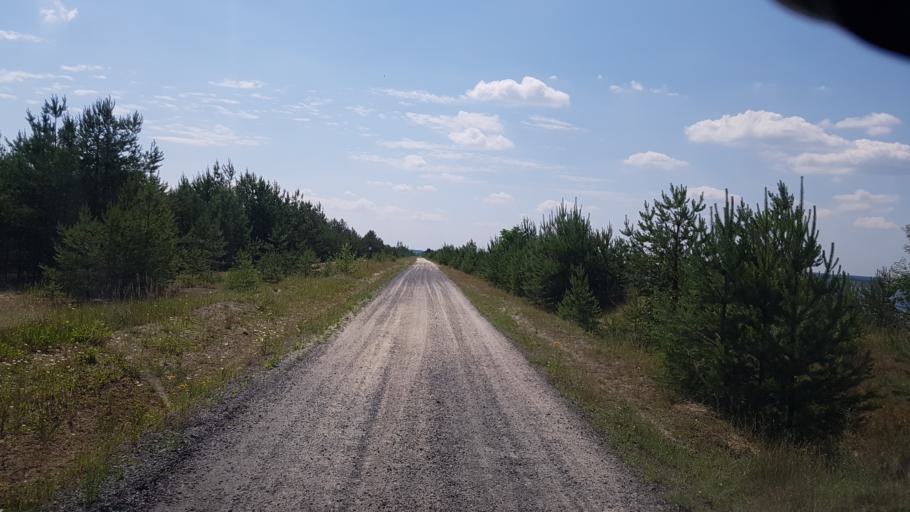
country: DE
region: Brandenburg
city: Sallgast
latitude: 51.5835
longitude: 13.7989
